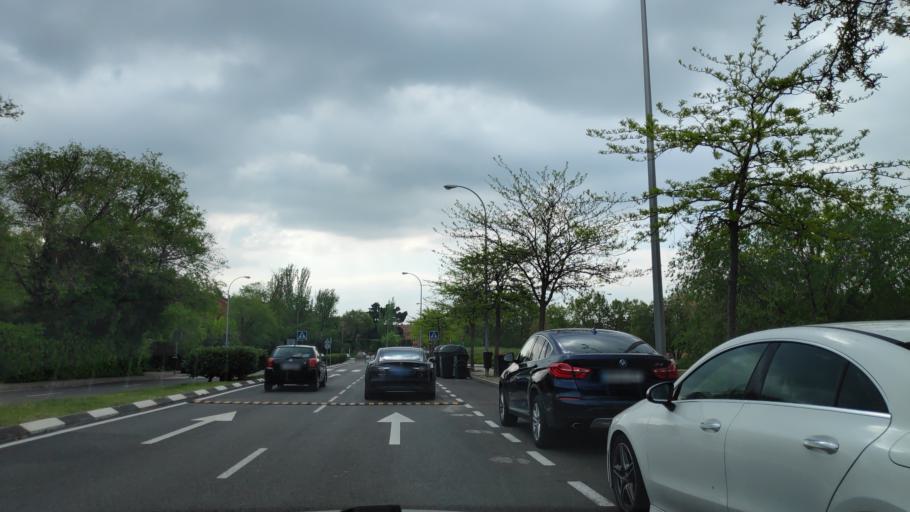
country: ES
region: Madrid
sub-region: Provincia de Madrid
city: Pozuelo de Alarcon
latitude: 40.4603
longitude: -3.7897
